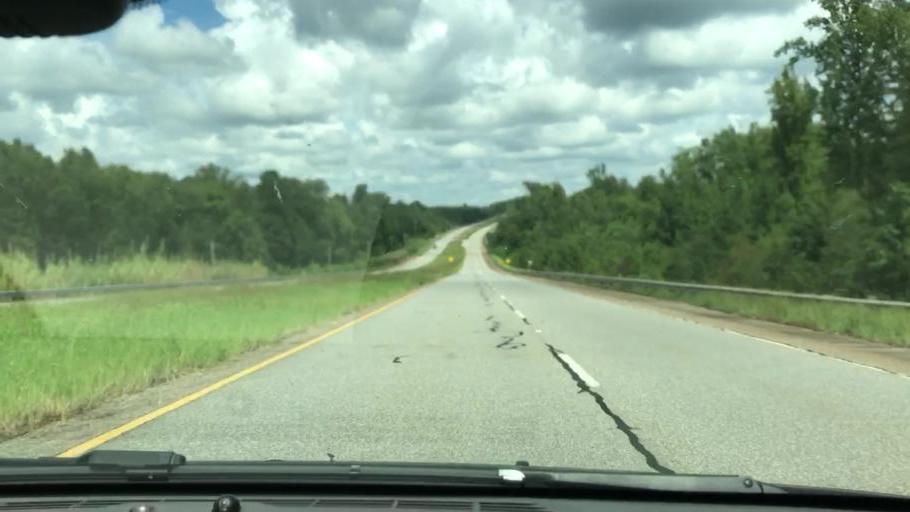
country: US
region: Georgia
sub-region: Stewart County
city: Lumpkin
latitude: 32.0994
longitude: -84.8105
